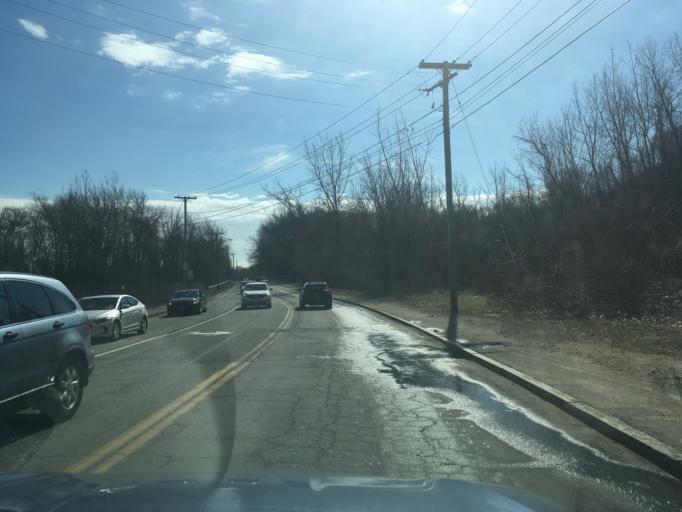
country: US
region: Rhode Island
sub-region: Providence County
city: Cranston
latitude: 41.7582
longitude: -71.4876
